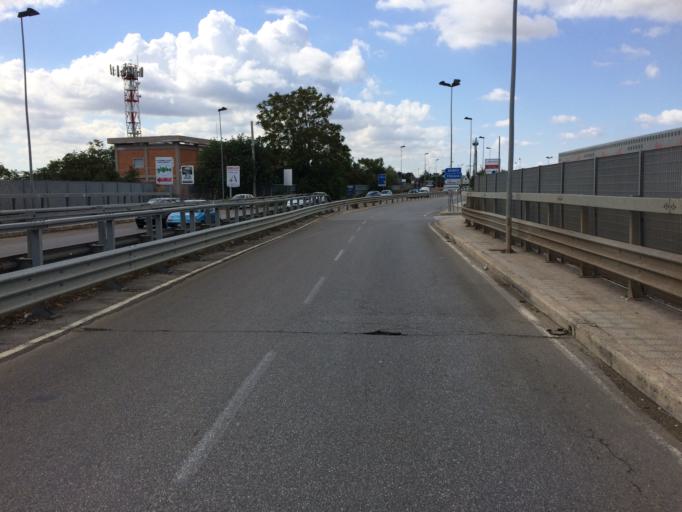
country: IT
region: Apulia
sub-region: Provincia di Bari
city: Bari
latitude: 41.0998
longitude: 16.8328
